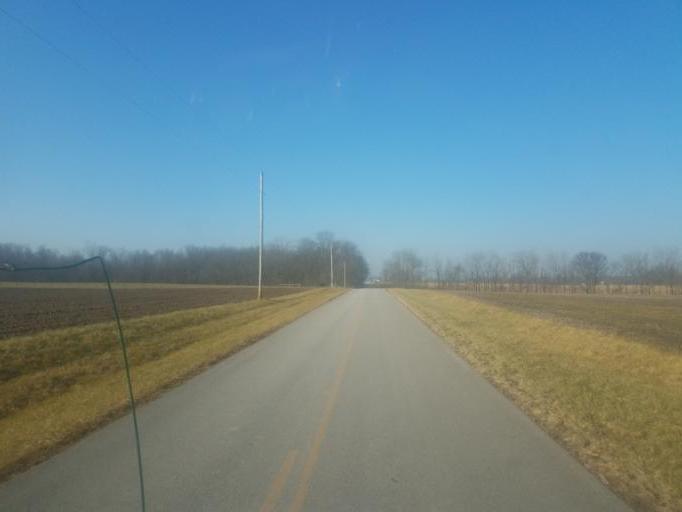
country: US
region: Ohio
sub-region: Seneca County
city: Tiffin
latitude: 41.0373
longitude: -82.9639
